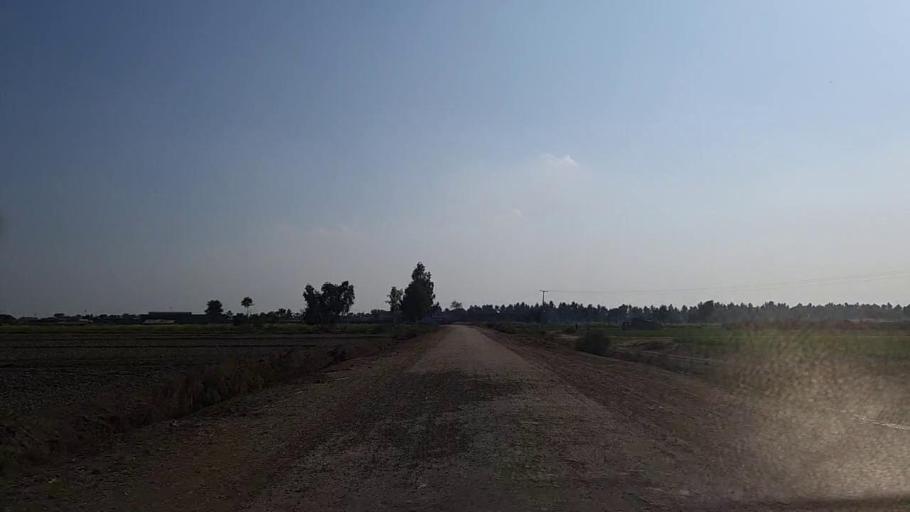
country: PK
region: Sindh
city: Jam Sahib
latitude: 26.2789
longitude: 68.5828
